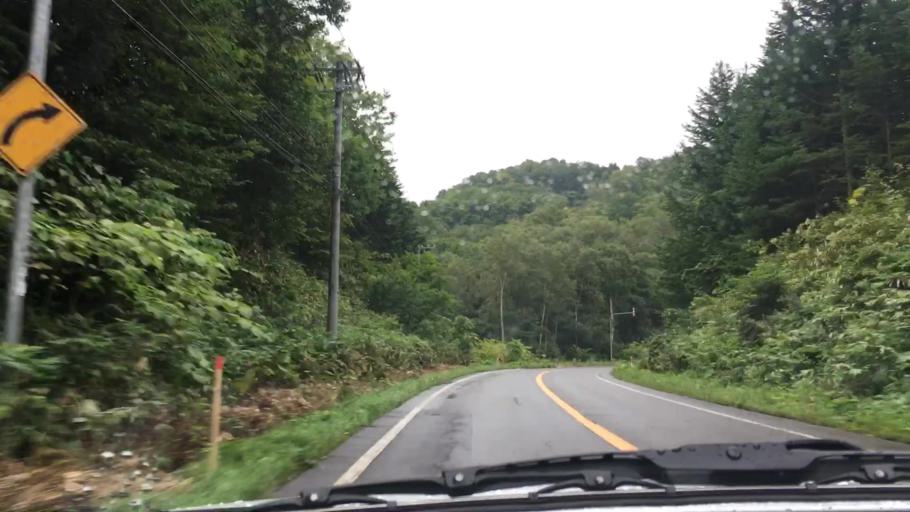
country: JP
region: Hokkaido
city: Niseko Town
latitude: 42.6155
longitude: 140.7292
